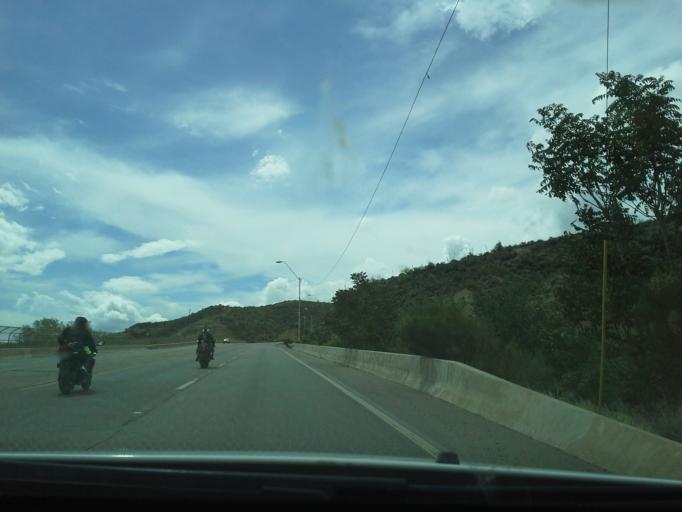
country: US
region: Arizona
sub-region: Gila County
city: Globe
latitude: 33.3954
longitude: -110.7890
